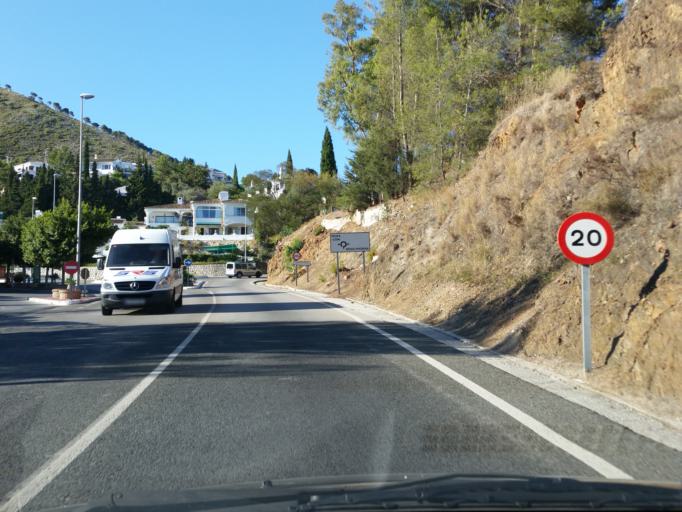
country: ES
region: Andalusia
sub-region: Provincia de Malaga
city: Mijas
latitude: 36.5988
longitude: -4.6319
